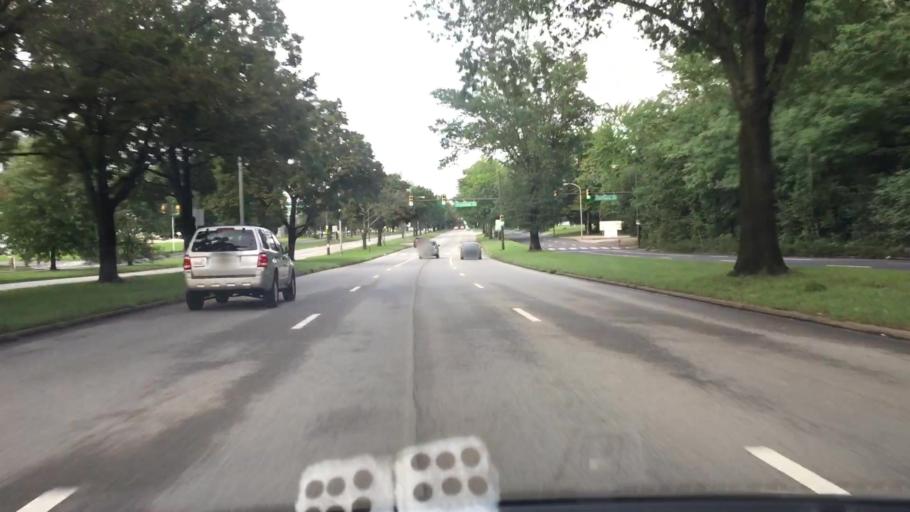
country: US
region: Pennsylvania
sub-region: Bucks County
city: Feasterville
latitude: 40.0969
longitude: -75.0129
